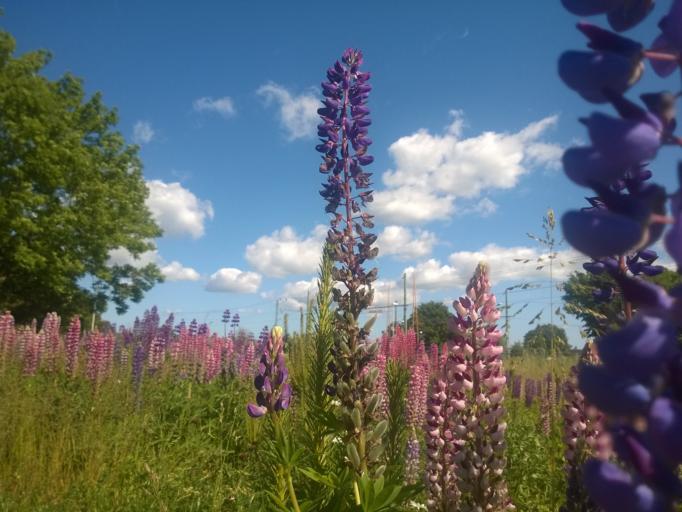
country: SE
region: Skane
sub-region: Kristianstads Kommun
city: Kristianstad
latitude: 56.0514
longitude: 14.1888
